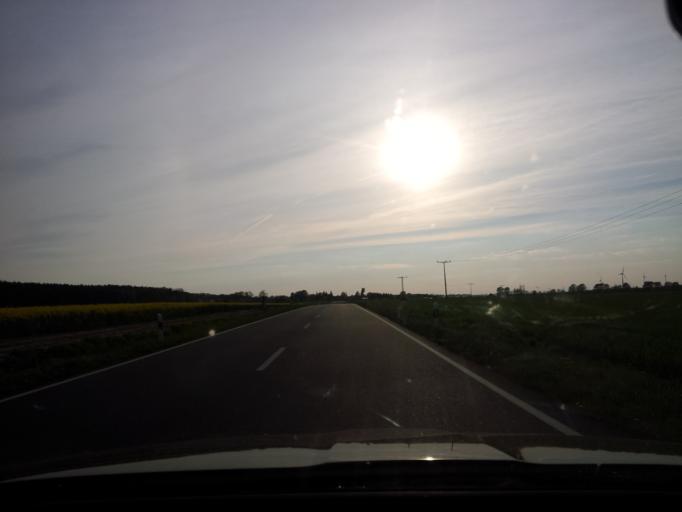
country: DE
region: Brandenburg
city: Drahnsdorf
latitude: 51.8492
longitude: 13.5479
